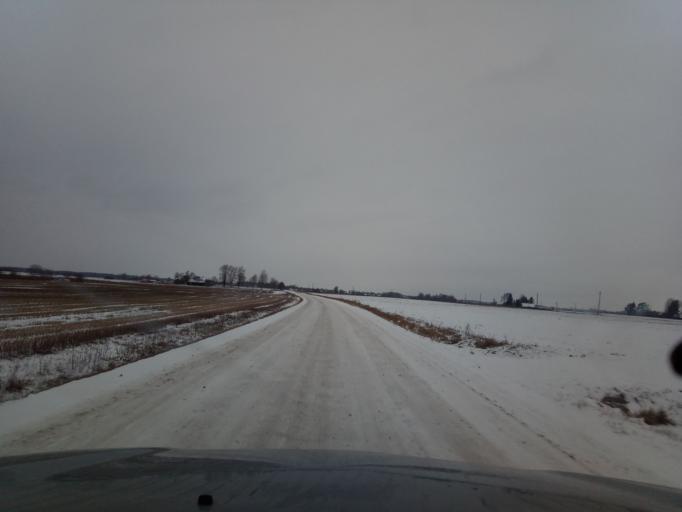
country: LT
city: Ramygala
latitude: 55.4961
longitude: 24.5248
